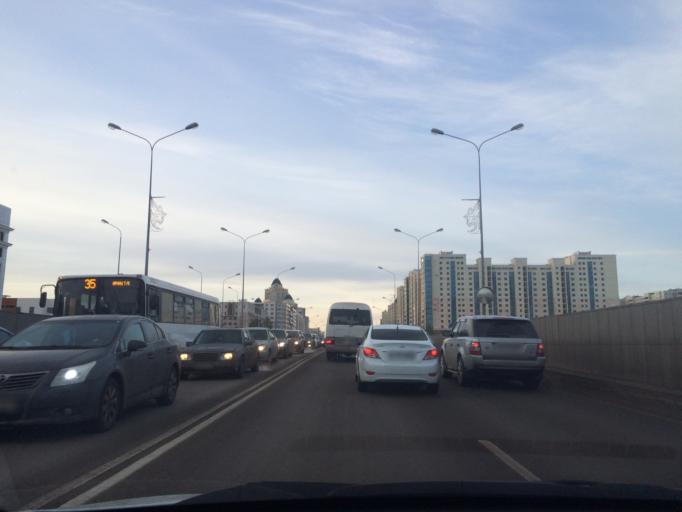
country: KZ
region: Astana Qalasy
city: Astana
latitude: 51.1203
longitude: 71.4358
